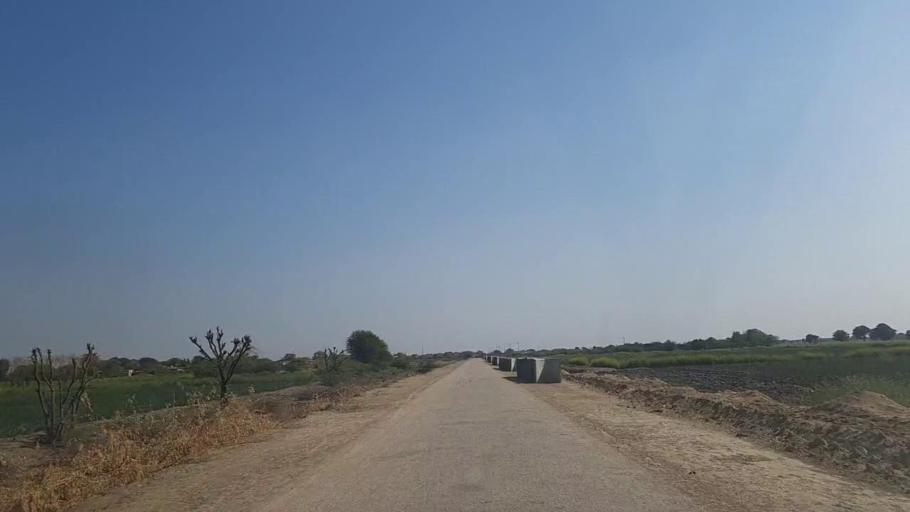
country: PK
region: Sindh
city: Digri
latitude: 25.1614
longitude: 69.1343
